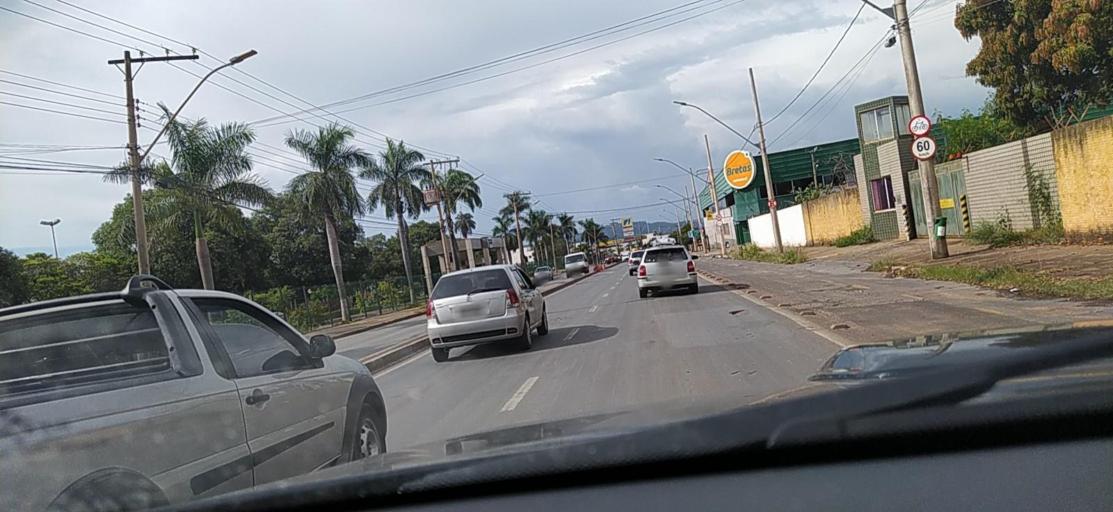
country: BR
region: Minas Gerais
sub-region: Montes Claros
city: Montes Claros
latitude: -16.7347
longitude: -43.8462
